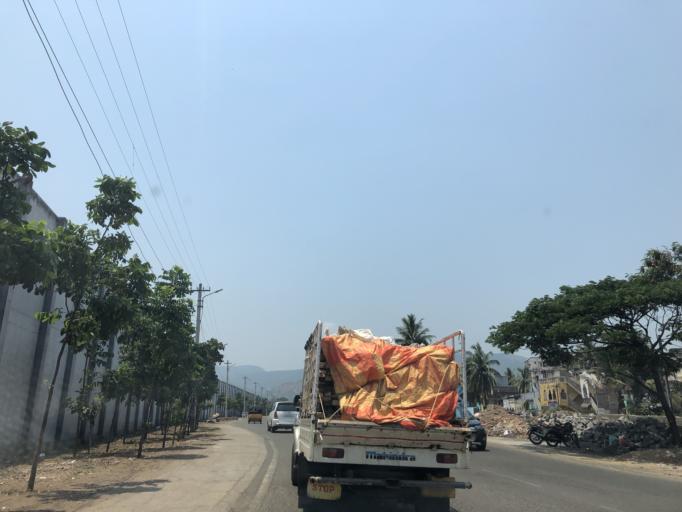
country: IN
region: Andhra Pradesh
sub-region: Vishakhapatnam
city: Yarada
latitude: 17.7125
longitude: 83.2933
